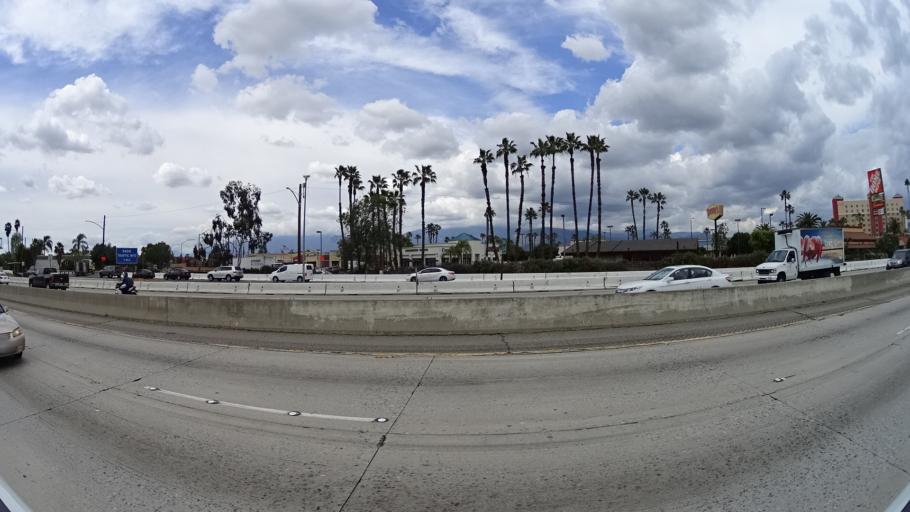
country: US
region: California
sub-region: Los Angeles County
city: Baldwin Park
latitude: 34.0703
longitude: -117.9589
